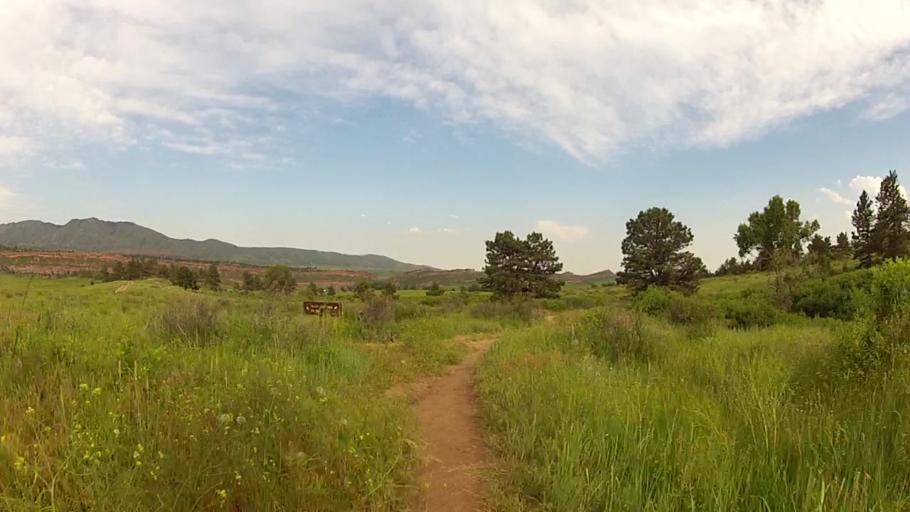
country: US
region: Colorado
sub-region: Larimer County
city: Laporte
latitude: 40.4864
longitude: -105.2390
